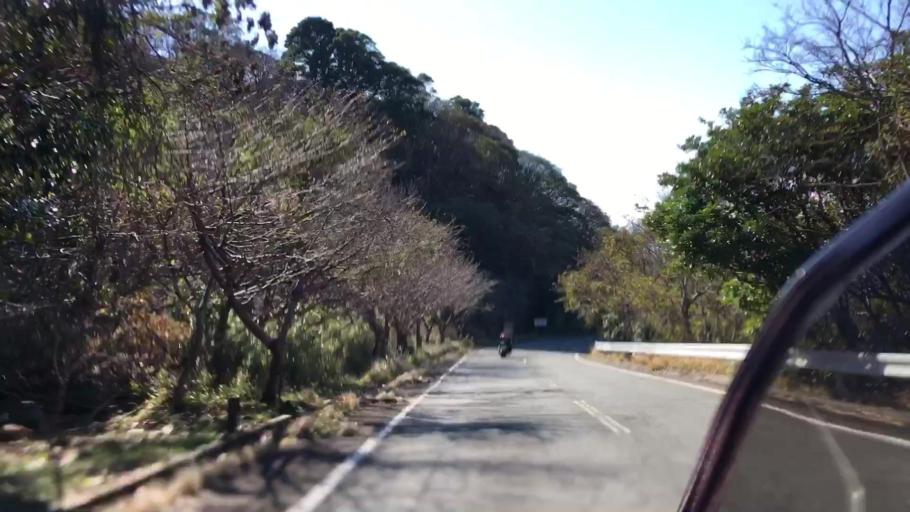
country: JP
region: Shizuoka
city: Heda
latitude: 35.0065
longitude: 138.7815
